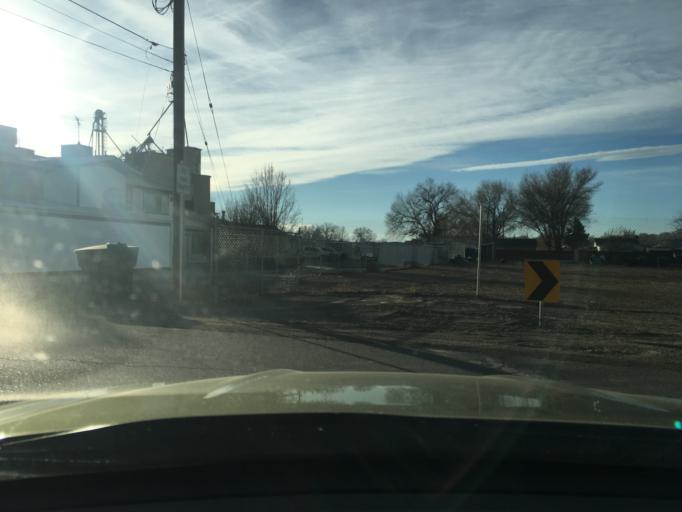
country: US
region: Colorado
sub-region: Delta County
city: Delta
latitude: 38.7417
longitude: -108.0778
